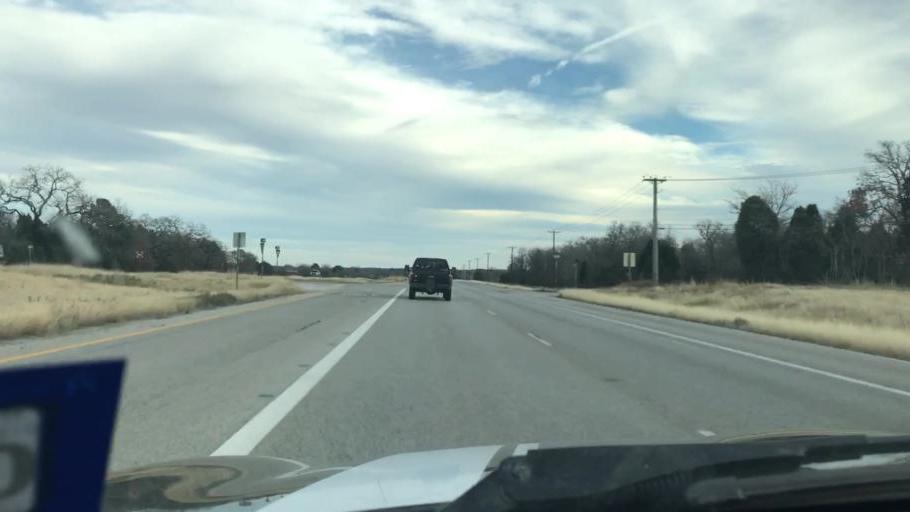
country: US
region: Texas
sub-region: Bastrop County
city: Elgin
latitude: 30.3231
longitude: -97.3236
